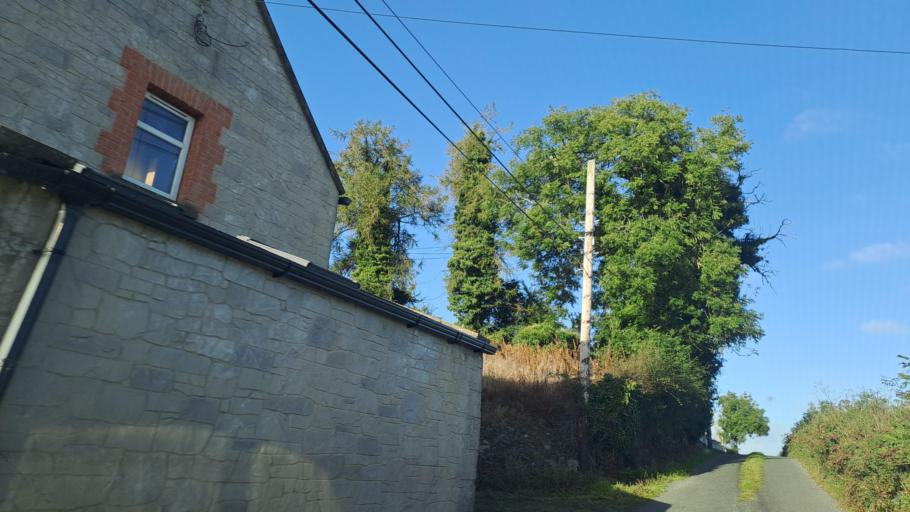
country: IE
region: Ulster
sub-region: An Cabhan
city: Kingscourt
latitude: 53.9891
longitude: -6.8687
